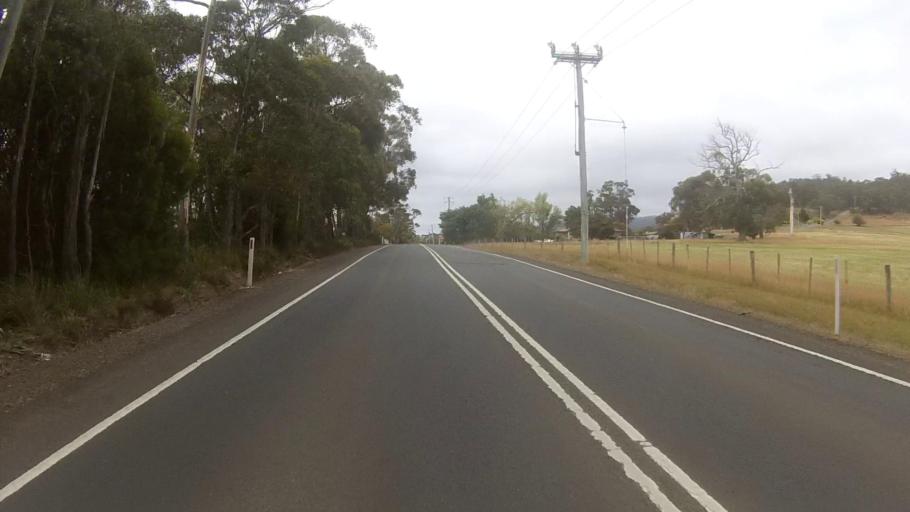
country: AU
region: Tasmania
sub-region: Kingborough
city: Margate
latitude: -42.9871
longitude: 147.1971
